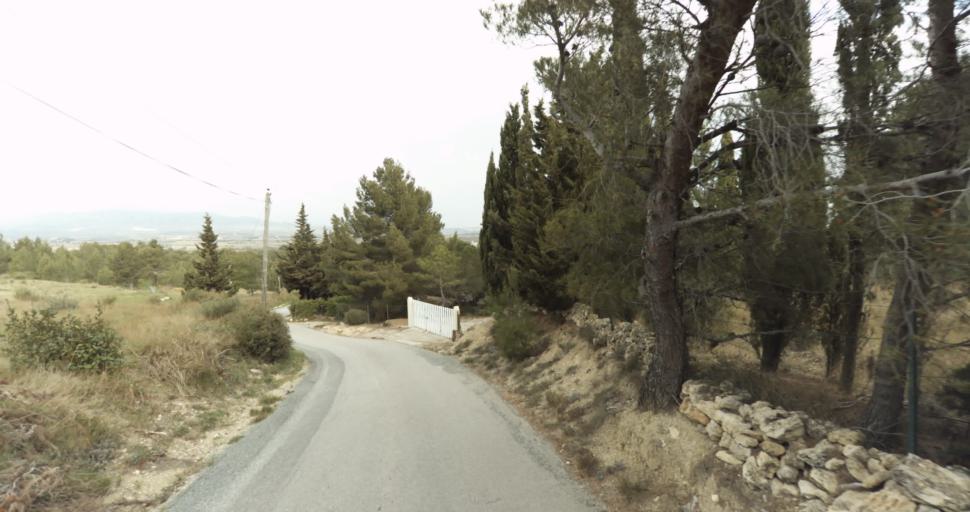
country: FR
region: Languedoc-Roussillon
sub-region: Departement de l'Aude
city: Leucate
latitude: 42.9327
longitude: 3.0231
